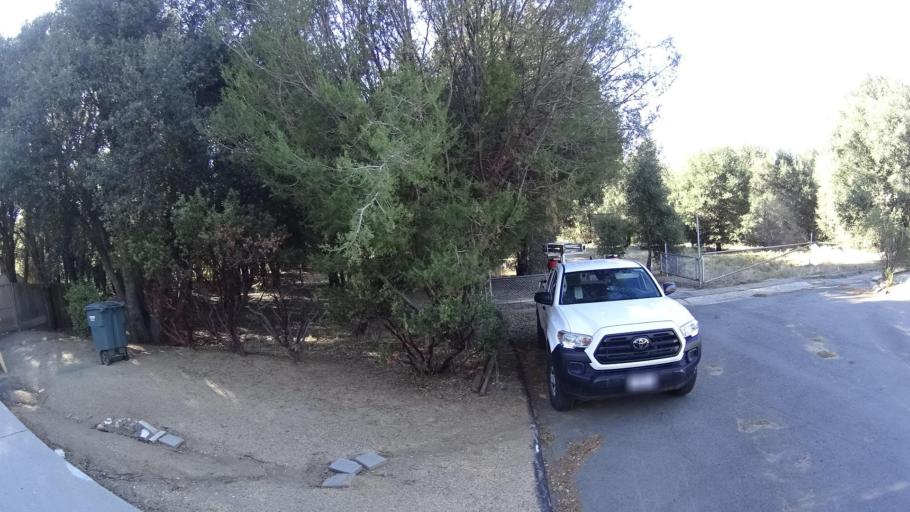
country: US
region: California
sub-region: San Diego County
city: Pine Valley
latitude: 32.8255
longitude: -116.5184
